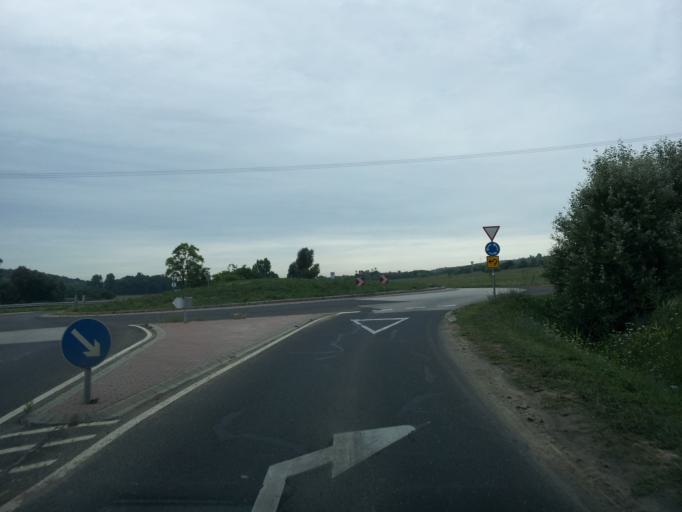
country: HU
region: Pest
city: Tarnok
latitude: 47.3925
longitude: 18.8490
